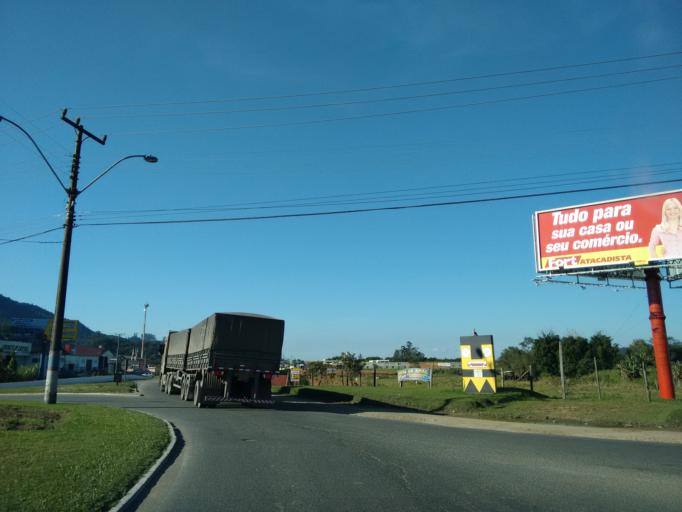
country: BR
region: Santa Catarina
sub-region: Guaramirim
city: Guaramirim
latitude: -26.4792
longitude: -49.0010
